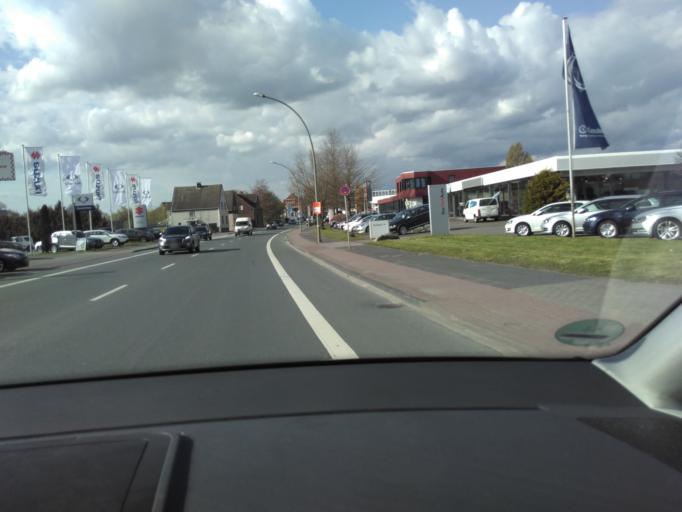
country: DE
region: North Rhine-Westphalia
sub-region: Regierungsbezirk Munster
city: Beckum
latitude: 51.7667
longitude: 8.0414
